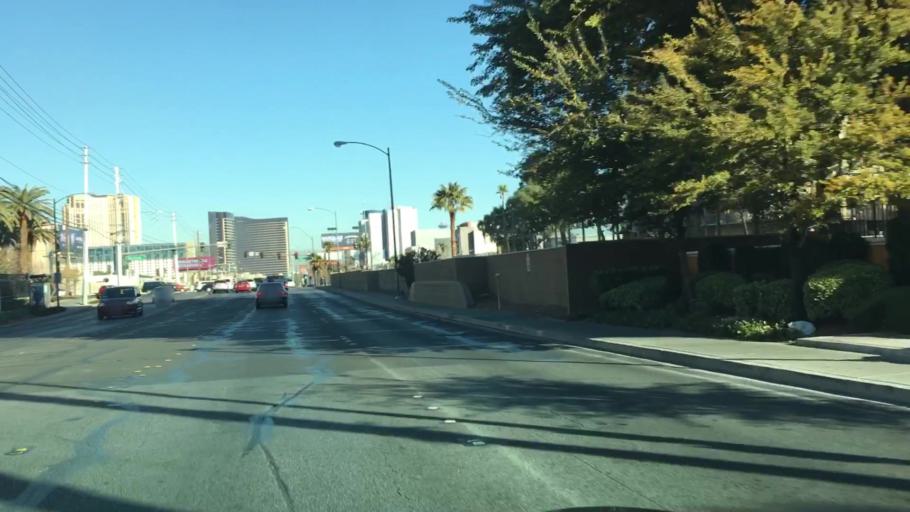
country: US
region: Nevada
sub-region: Clark County
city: Paradise
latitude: 36.1068
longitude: -115.1639
